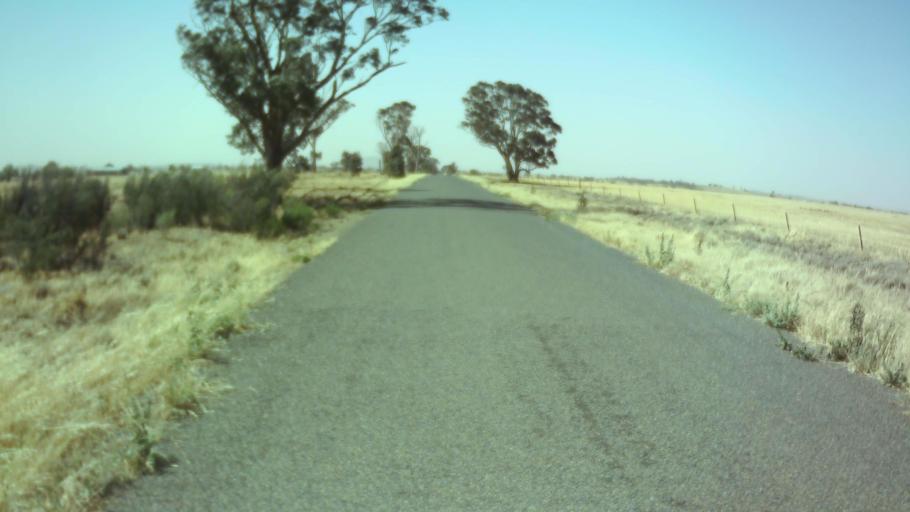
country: AU
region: New South Wales
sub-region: Weddin
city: Grenfell
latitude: -33.8833
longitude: 147.9240
